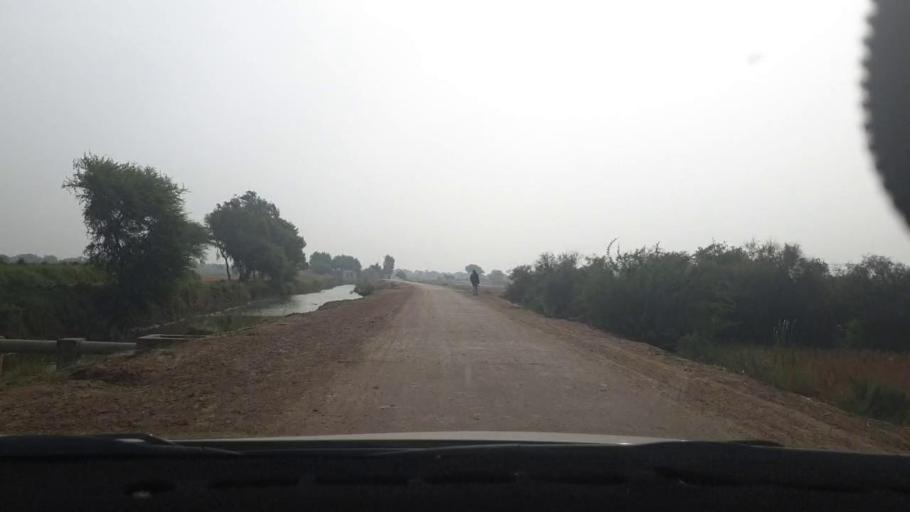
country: PK
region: Sindh
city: Tando Muhammad Khan
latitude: 25.0556
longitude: 68.5474
